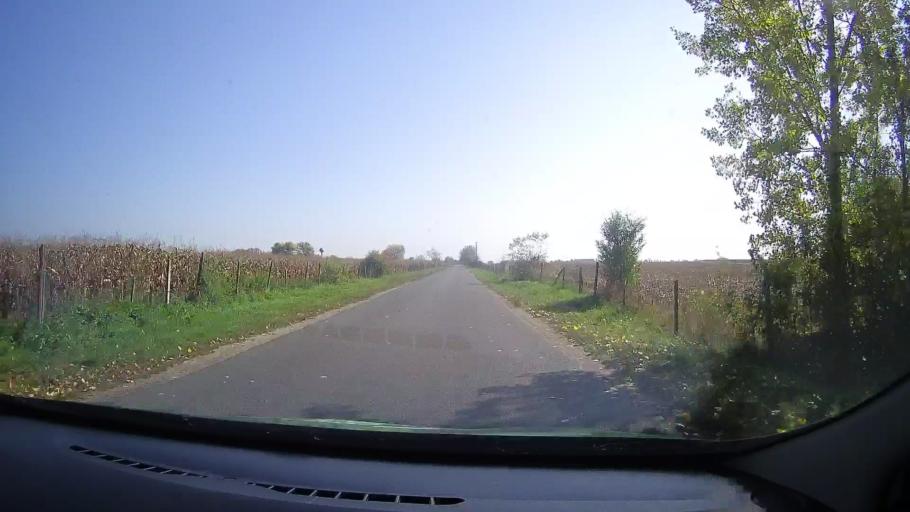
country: RO
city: Foieni
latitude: 47.6972
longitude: 22.3610
